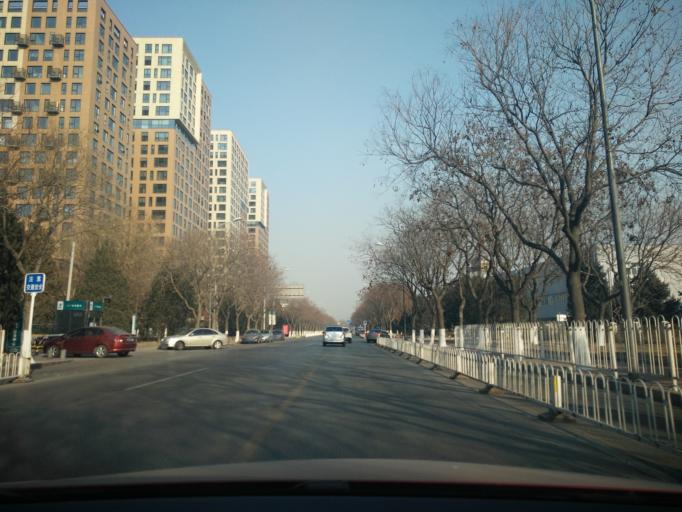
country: CN
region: Beijing
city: Jiugong
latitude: 39.8079
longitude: 116.5011
